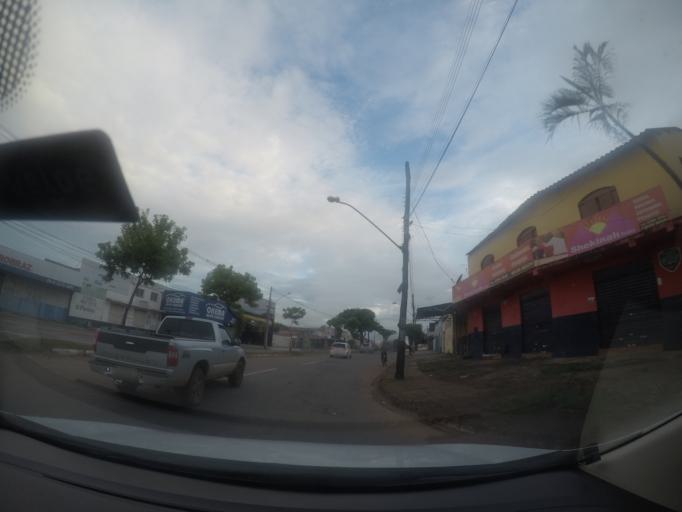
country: BR
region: Goias
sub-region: Goiania
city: Goiania
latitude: -16.6834
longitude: -49.3206
